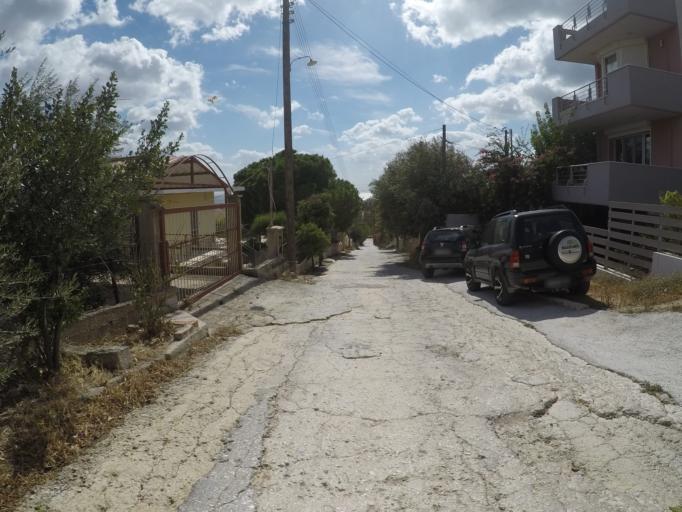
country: GR
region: Attica
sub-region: Nomarchia Anatolikis Attikis
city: Agios Dimitrios Kropias
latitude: 37.7978
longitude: 23.8774
